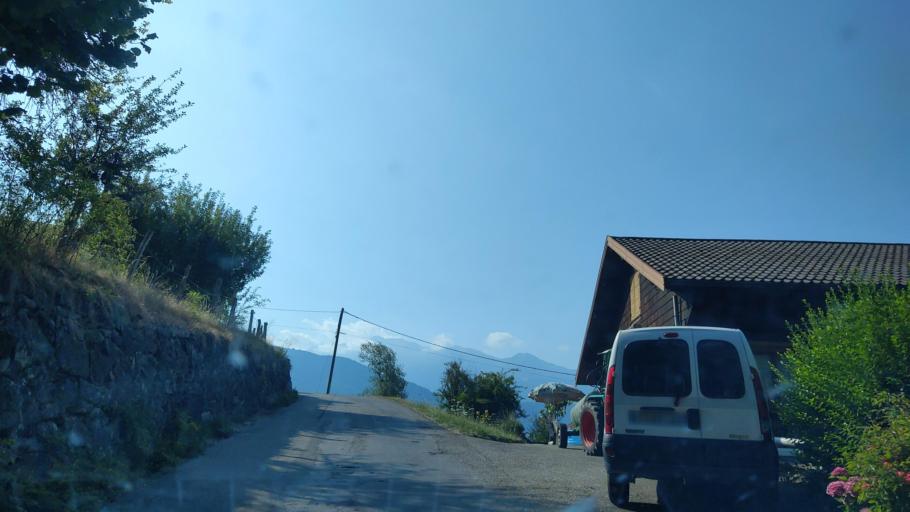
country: FR
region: Rhone-Alpes
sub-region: Departement de la Savoie
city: Ugine
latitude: 45.7705
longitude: 6.4013
